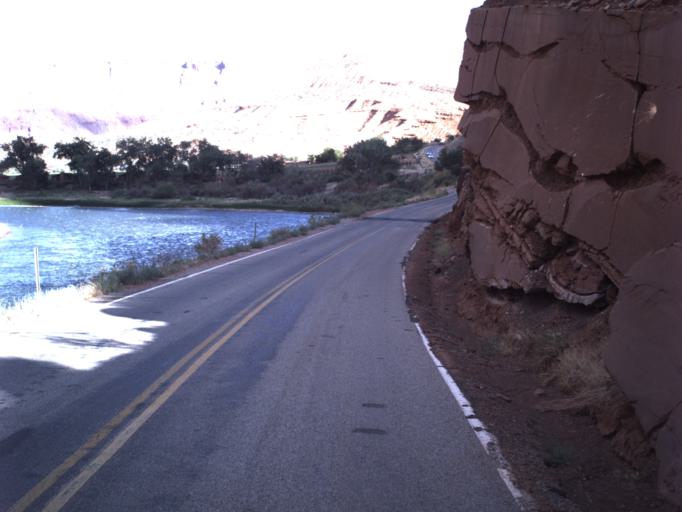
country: US
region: Utah
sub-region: Grand County
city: Moab
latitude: 38.6832
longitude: -109.4573
